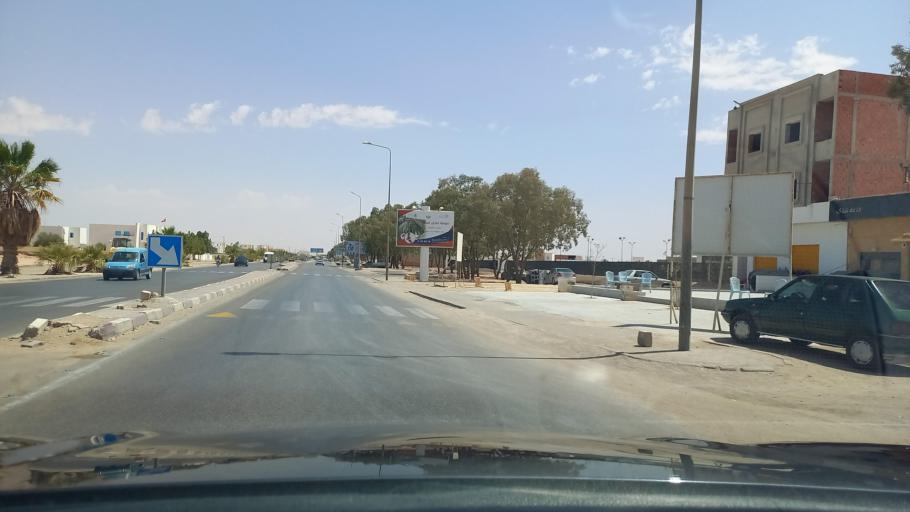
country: TN
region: Madanin
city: Medenine
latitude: 33.3630
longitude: 10.4634
